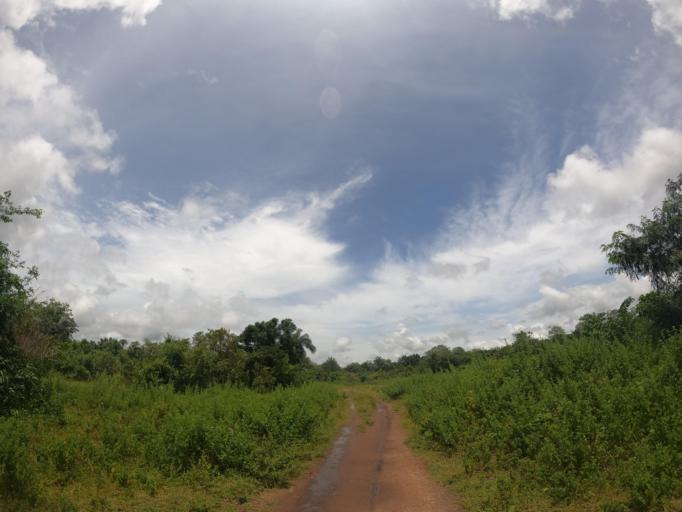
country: SL
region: Northern Province
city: Binkolo
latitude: 9.1374
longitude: -12.2377
